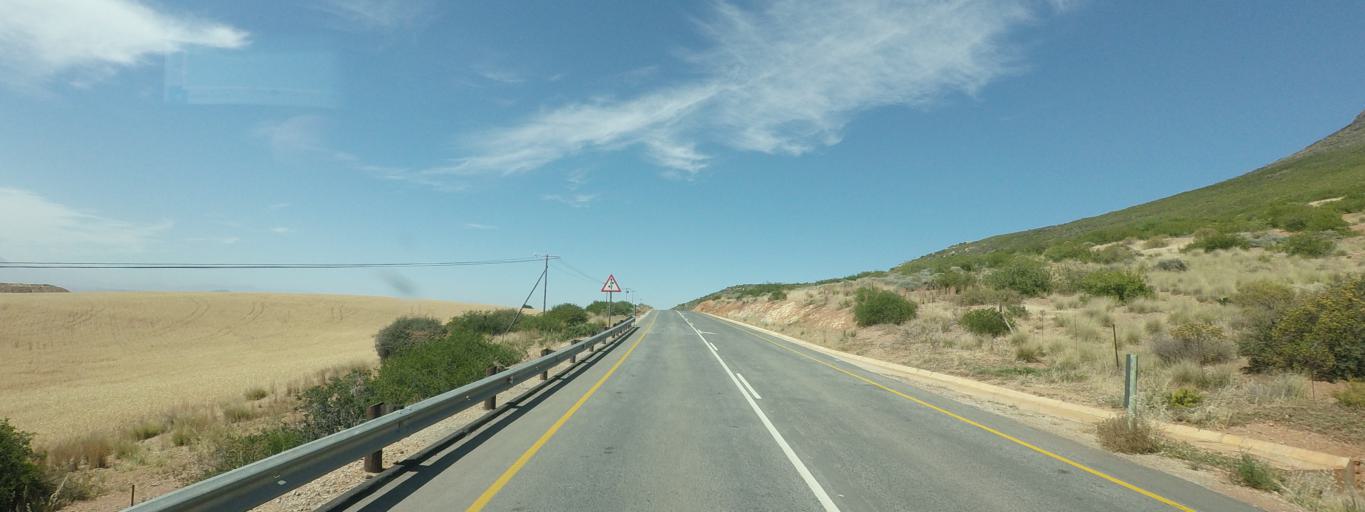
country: ZA
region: Western Cape
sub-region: West Coast District Municipality
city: Piketberg
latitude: -32.9261
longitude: 18.7561
